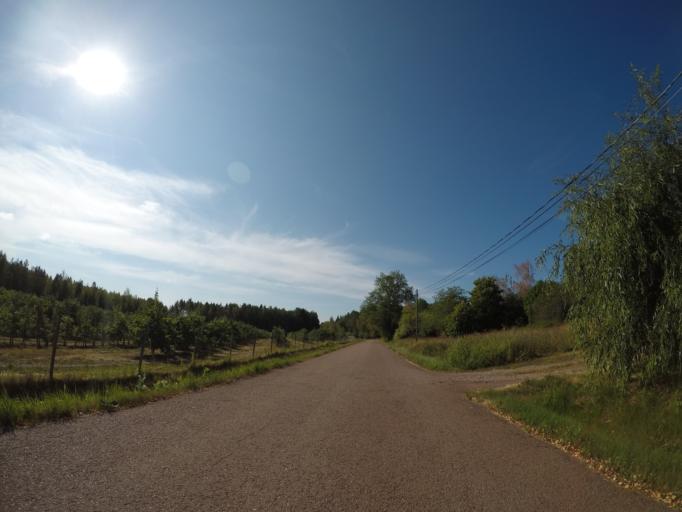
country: AX
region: Alands landsbygd
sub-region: Finstroem
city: Finstroem
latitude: 60.2793
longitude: 19.9172
